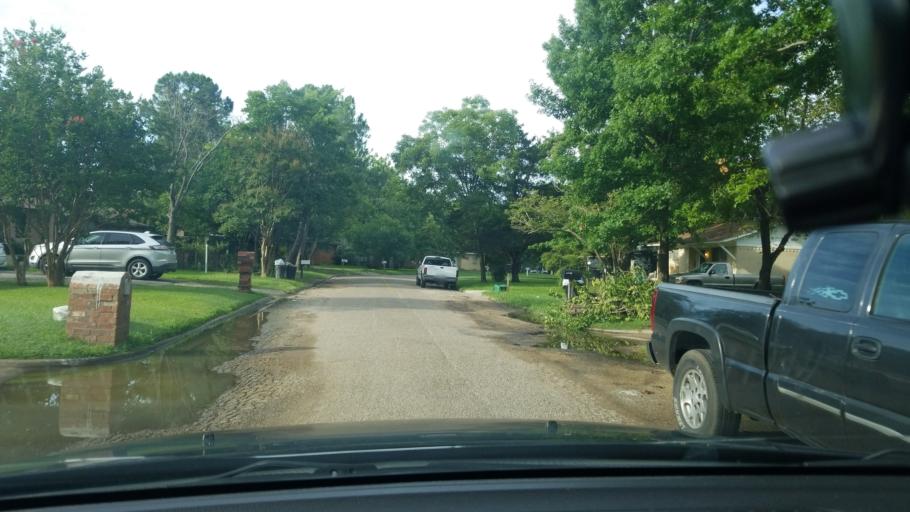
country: US
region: Texas
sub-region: Dallas County
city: Balch Springs
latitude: 32.7551
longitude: -96.6260
